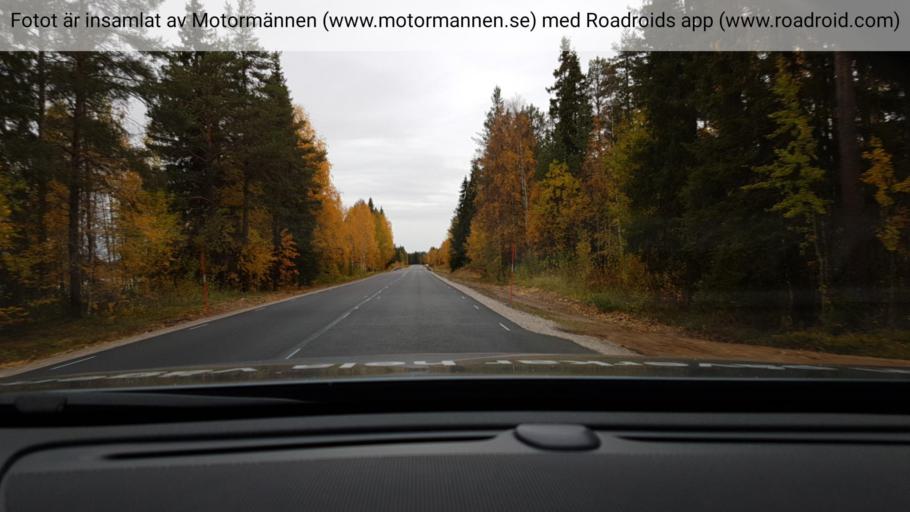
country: SE
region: Norrbotten
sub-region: Overkalix Kommun
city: OEverkalix
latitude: 66.4103
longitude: 22.8053
